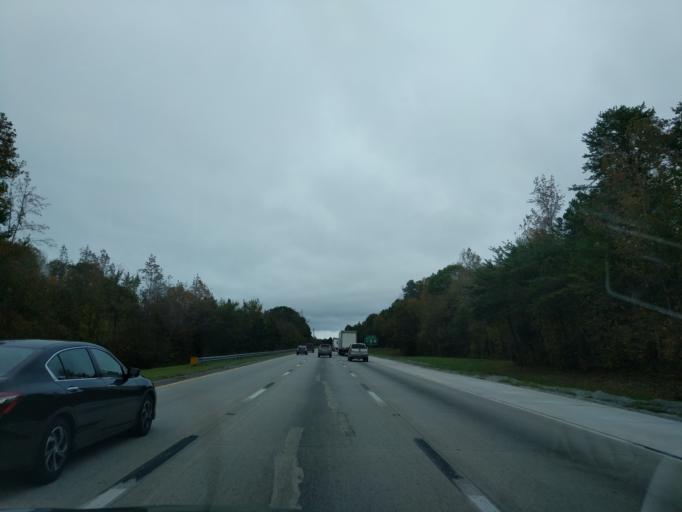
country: US
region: North Carolina
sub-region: Guilford County
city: Jamestown
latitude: 35.9724
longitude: -79.8906
